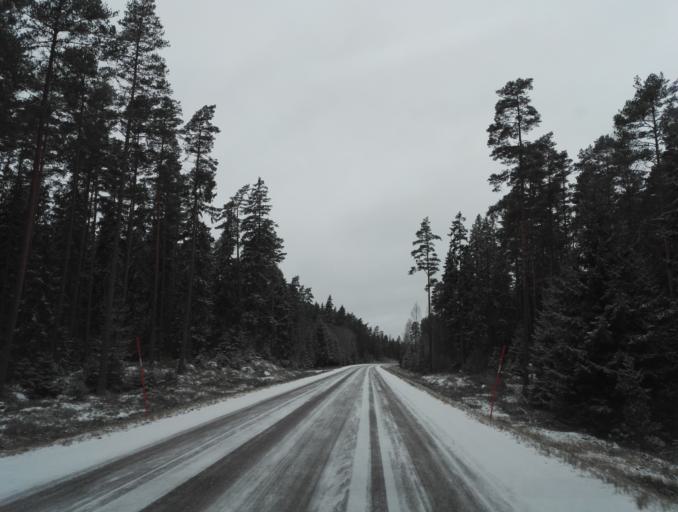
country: SE
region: Kronoberg
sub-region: Lessebo Kommun
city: Lessebo
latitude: 56.7319
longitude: 15.2288
